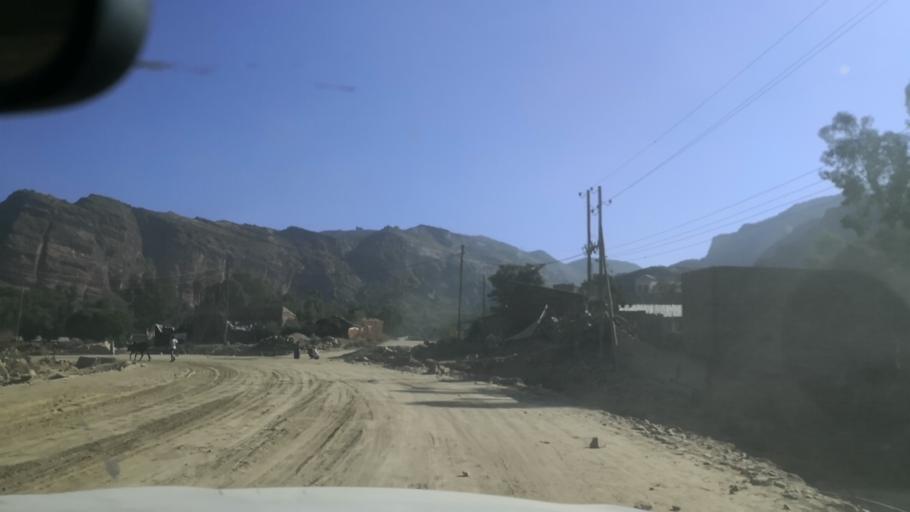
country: ET
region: Tigray
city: Mekele
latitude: 13.8460
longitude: 39.5340
